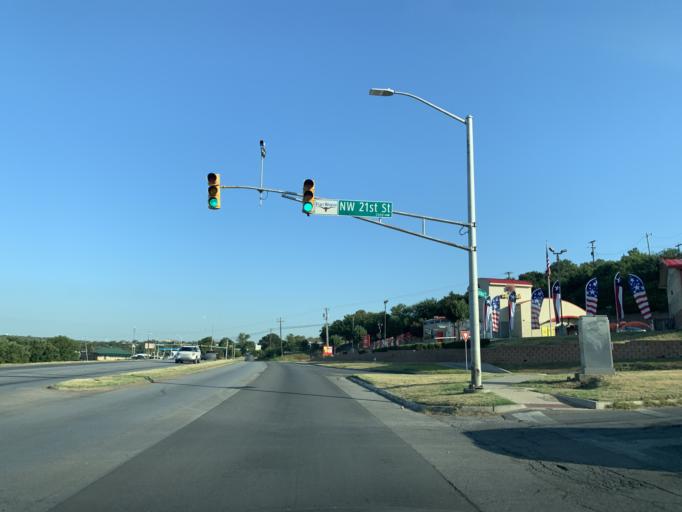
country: US
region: Texas
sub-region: Tarrant County
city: River Oaks
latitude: 32.7800
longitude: -97.3705
